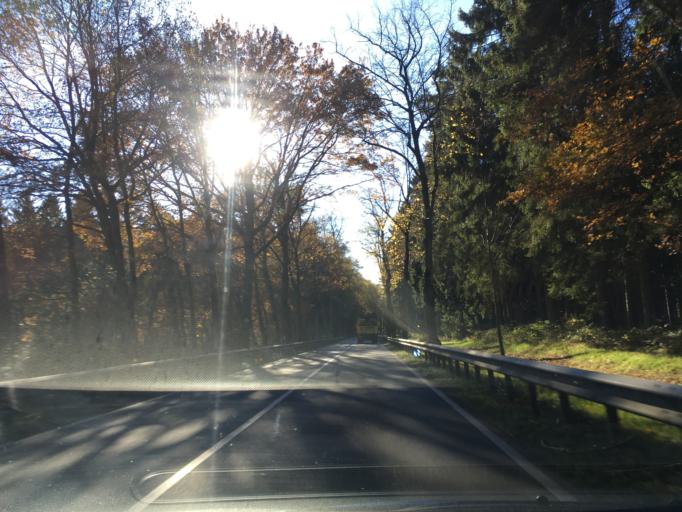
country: DE
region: Lower Saxony
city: Soderstorf
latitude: 53.1076
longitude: 10.1722
